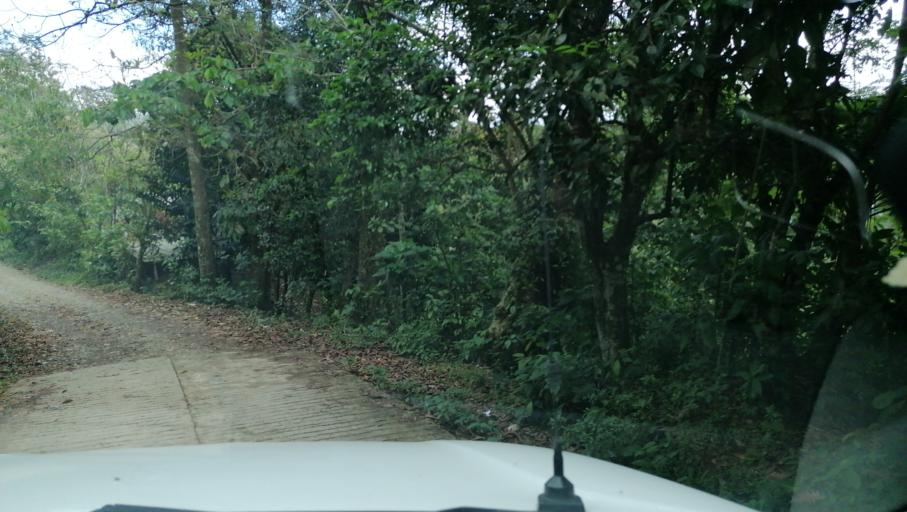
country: MX
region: Chiapas
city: Ixtacomitan
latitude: 17.3567
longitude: -93.1167
